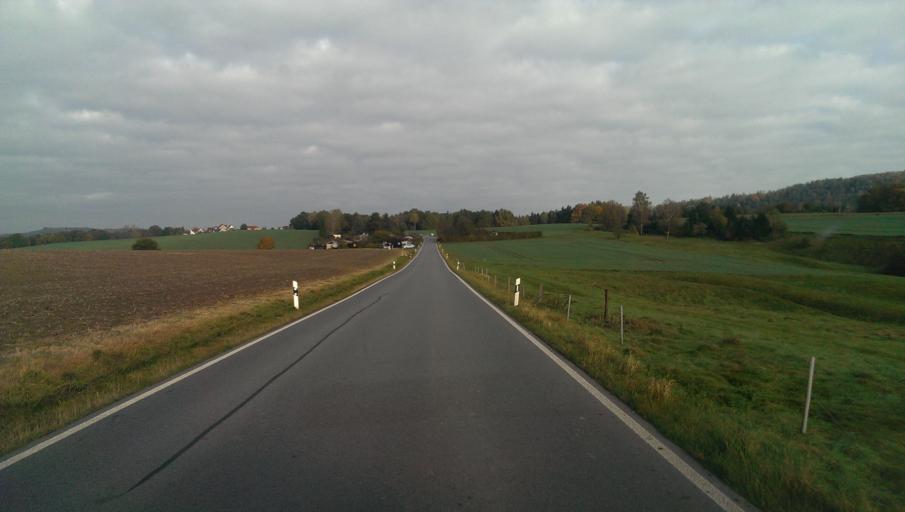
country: DE
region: Saxony
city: Porschdorf
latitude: 50.9447
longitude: 14.1203
